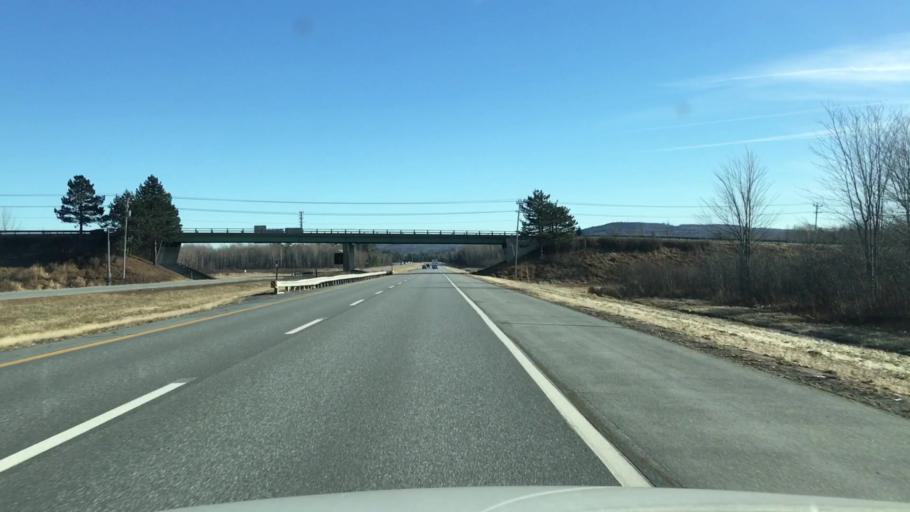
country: US
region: Maine
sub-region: Penobscot County
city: Brewer
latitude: 44.7746
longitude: -68.7477
